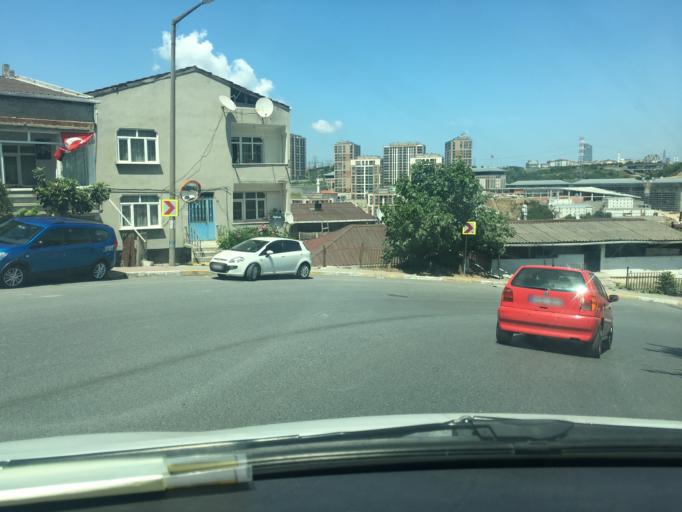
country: TR
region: Istanbul
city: Sisli
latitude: 41.0844
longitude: 28.9452
